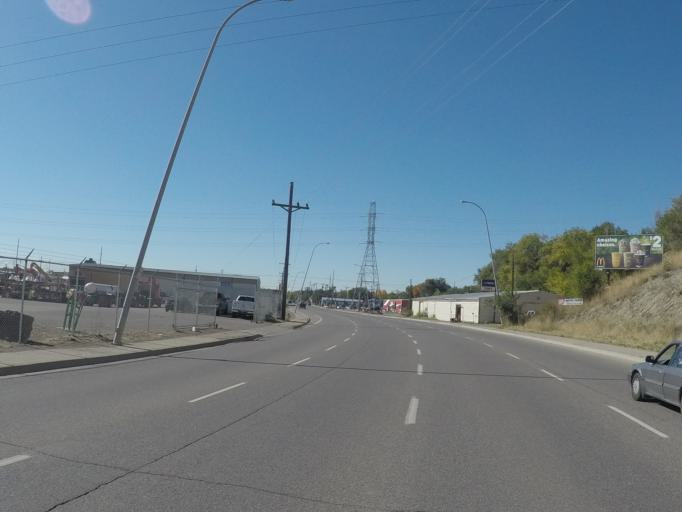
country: US
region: Montana
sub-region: Yellowstone County
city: Billings
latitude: 45.7966
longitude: -108.4886
